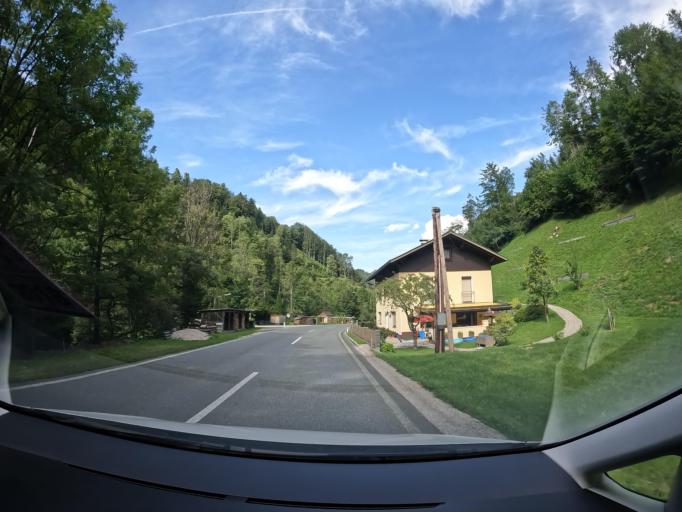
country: AT
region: Carinthia
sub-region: Politischer Bezirk Volkermarkt
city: Bad Eisenkappel
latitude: 46.4483
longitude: 14.5895
